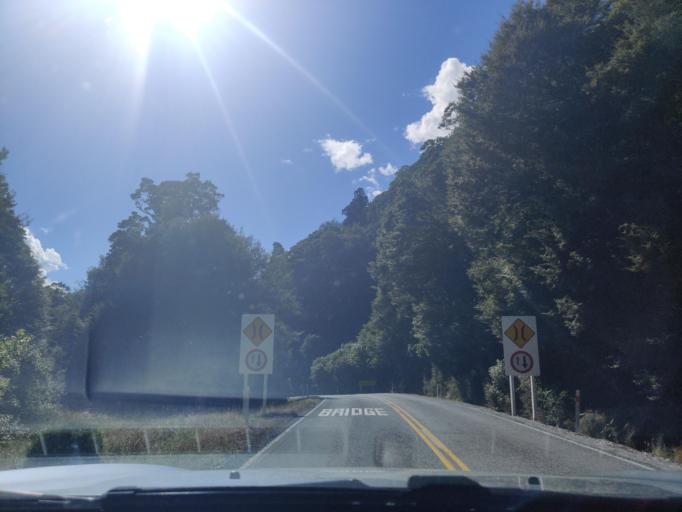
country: NZ
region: Otago
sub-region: Queenstown-Lakes District
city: Wanaka
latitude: -44.0142
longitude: 169.3842
